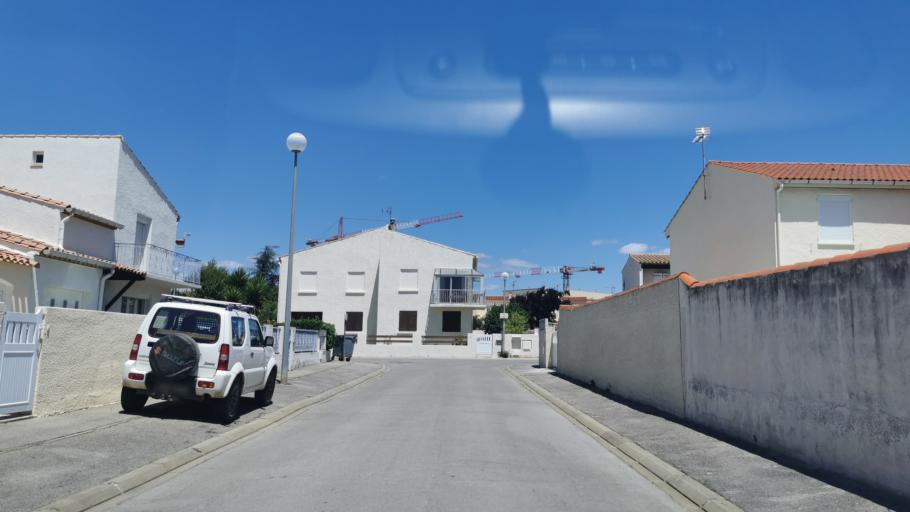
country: FR
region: Languedoc-Roussillon
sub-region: Departement de l'Aude
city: Narbonne
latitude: 43.1872
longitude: 3.0212
